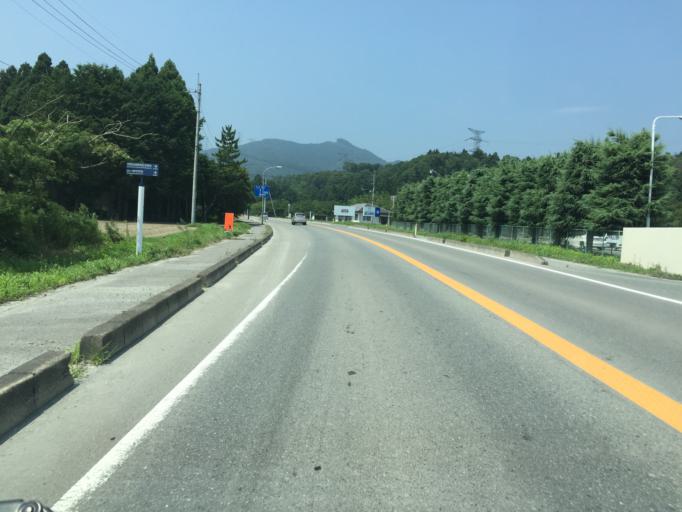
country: JP
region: Miyagi
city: Marumori
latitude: 37.8478
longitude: 140.8869
